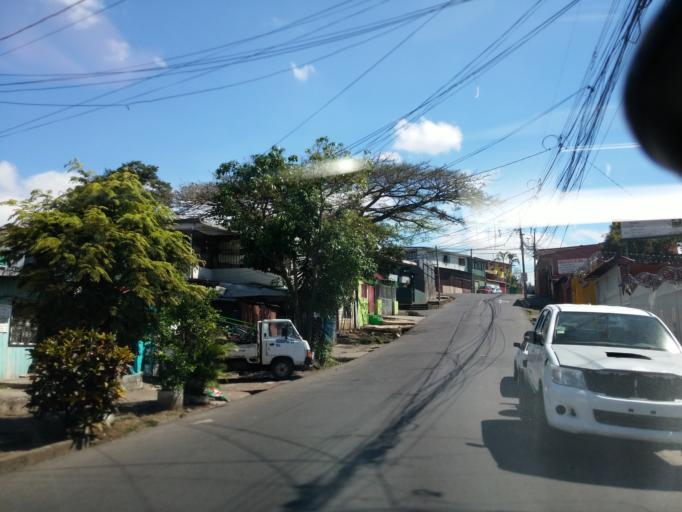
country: CR
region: San Jose
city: San Jose
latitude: 9.9169
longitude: -84.0840
